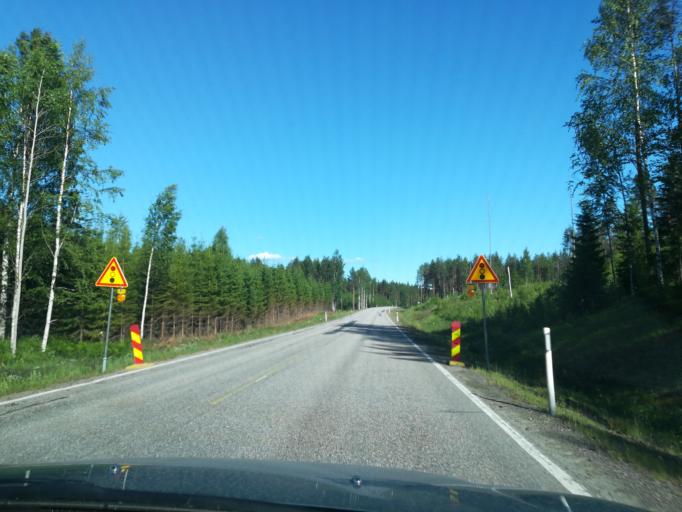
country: FI
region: Southern Savonia
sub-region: Mikkeli
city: Puumala
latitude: 61.4710
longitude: 28.3074
